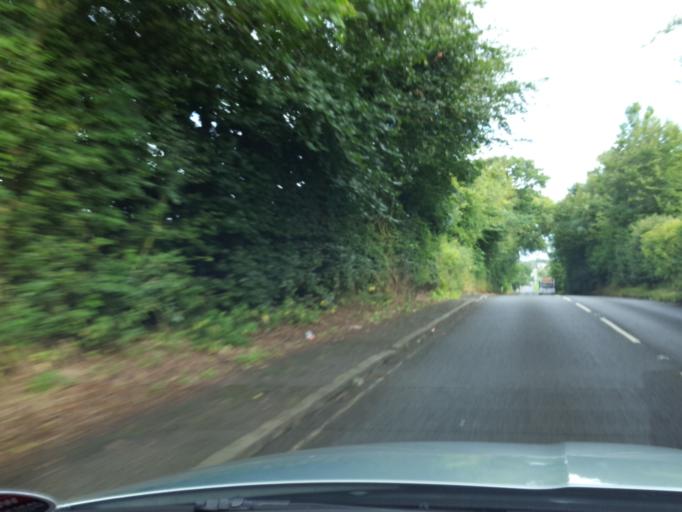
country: GB
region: Scotland
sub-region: Falkirk
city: Bo'ness
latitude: 56.0003
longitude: -3.6087
